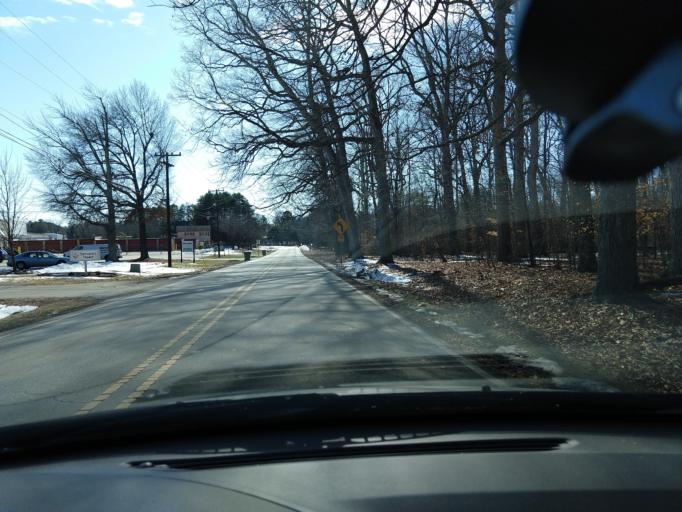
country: US
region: North Carolina
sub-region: Guilford County
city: Greensboro
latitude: 36.1290
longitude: -79.8458
